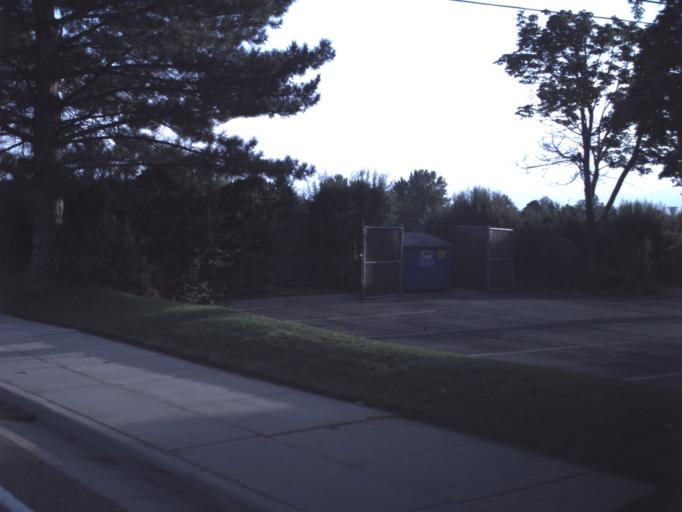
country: US
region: Utah
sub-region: Salt Lake County
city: Midvale
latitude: 40.6327
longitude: -111.8896
